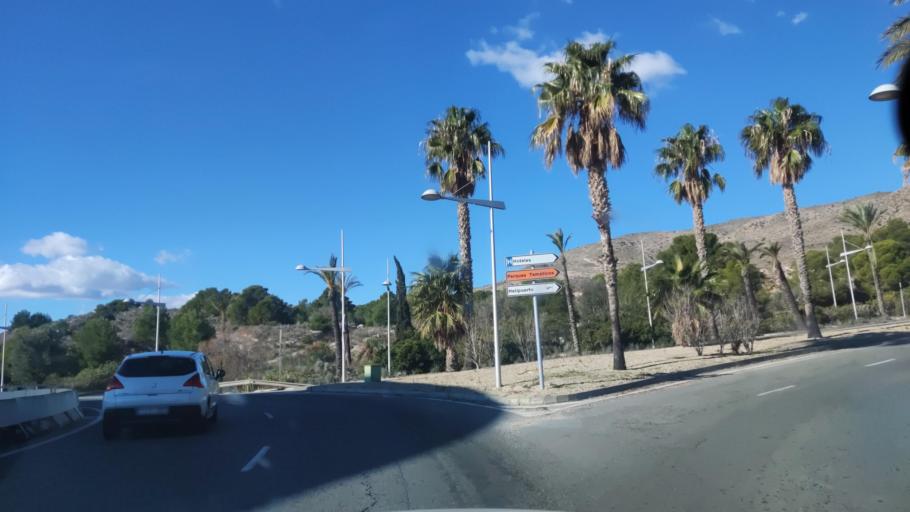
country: ES
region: Valencia
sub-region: Provincia de Alicante
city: Benidorm
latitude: 38.5501
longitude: -0.1631
